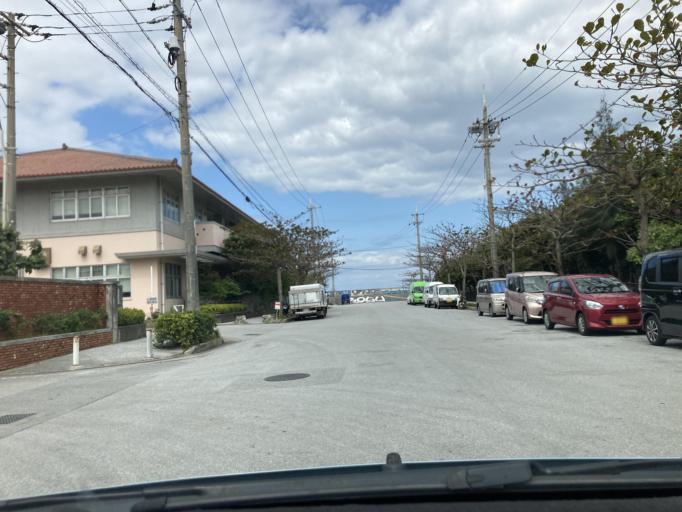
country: JP
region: Okinawa
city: Naha-shi
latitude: 26.2496
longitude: 127.6732
